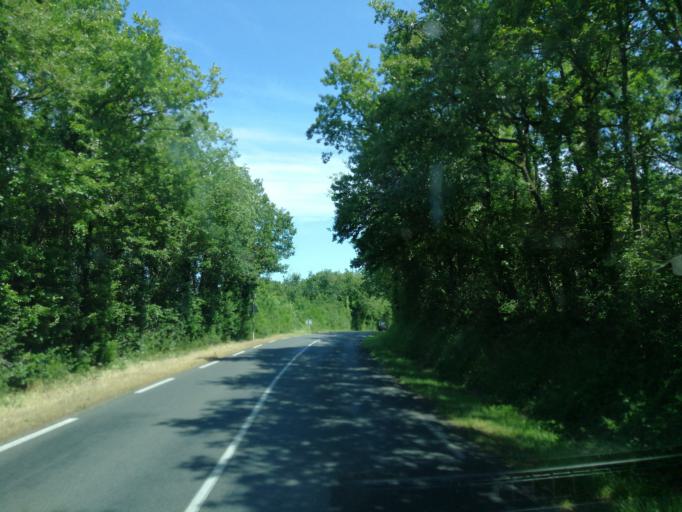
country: FR
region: Poitou-Charentes
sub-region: Departement des Deux-Sevres
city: Saint-Jean-de-Thouars
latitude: 46.9735
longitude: -0.1731
